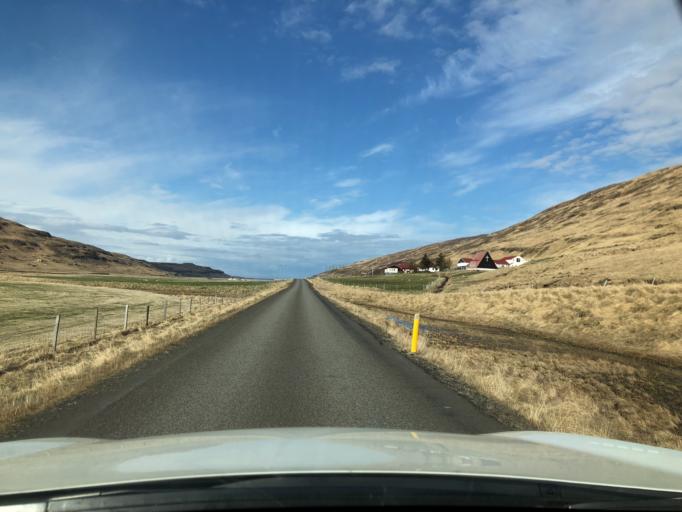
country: IS
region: West
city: Borgarnes
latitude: 65.0581
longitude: -21.5420
